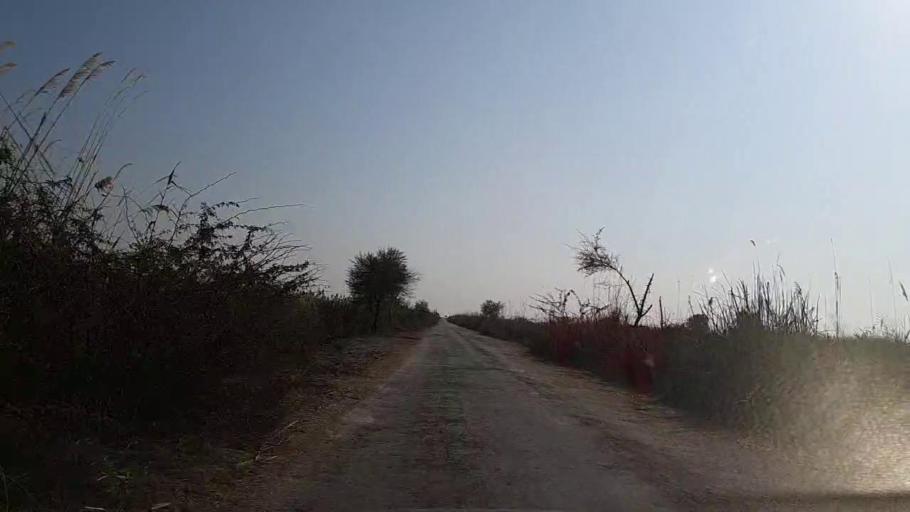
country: PK
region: Sindh
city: Tando Mittha Khan
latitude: 25.8956
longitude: 69.0770
